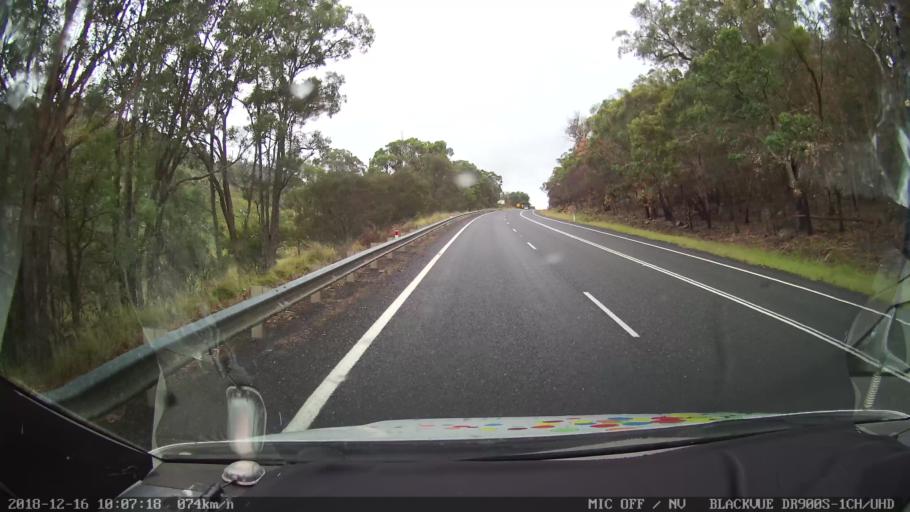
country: AU
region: New South Wales
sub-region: Glen Innes Severn
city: Glen Innes
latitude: -29.3363
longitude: 151.8952
